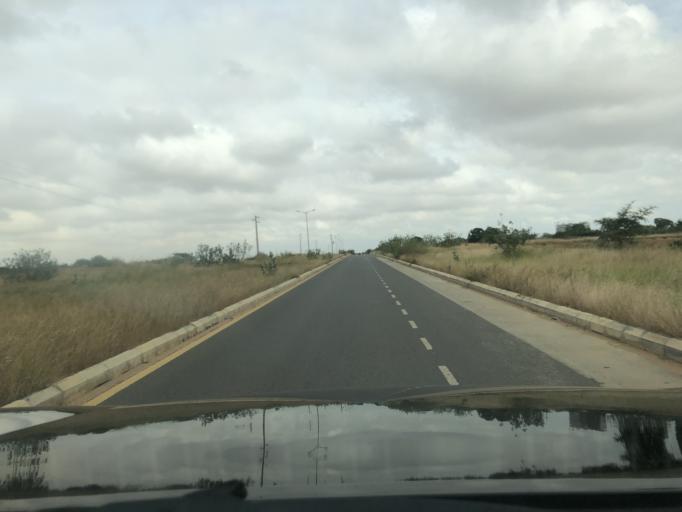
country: AO
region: Luanda
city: Luanda
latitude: -8.9546
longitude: 13.2530
